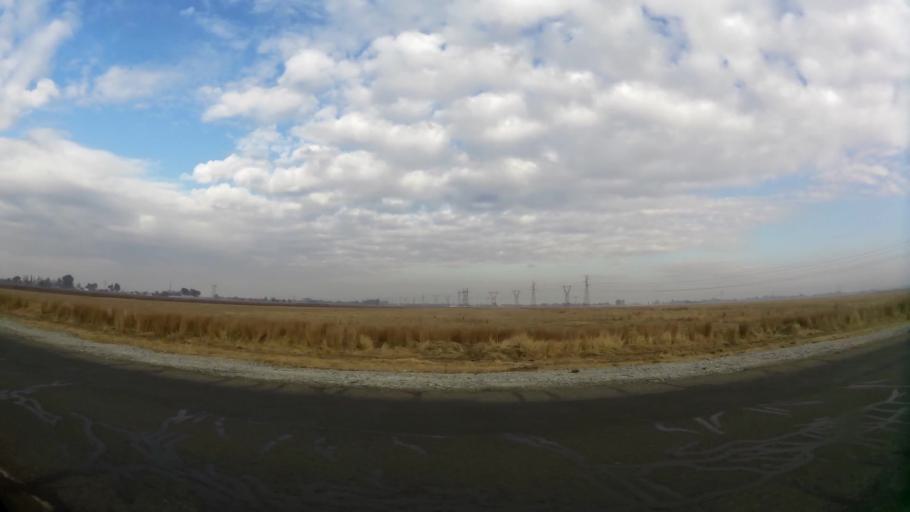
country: ZA
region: Gauteng
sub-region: Sedibeng District Municipality
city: Vanderbijlpark
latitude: -26.6685
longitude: 27.7885
